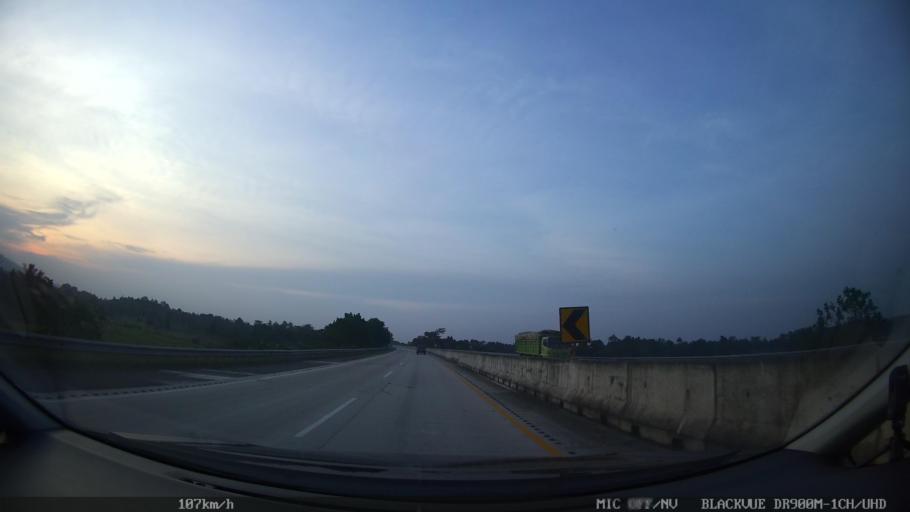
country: ID
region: Lampung
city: Penengahan
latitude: -5.7537
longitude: 105.7089
